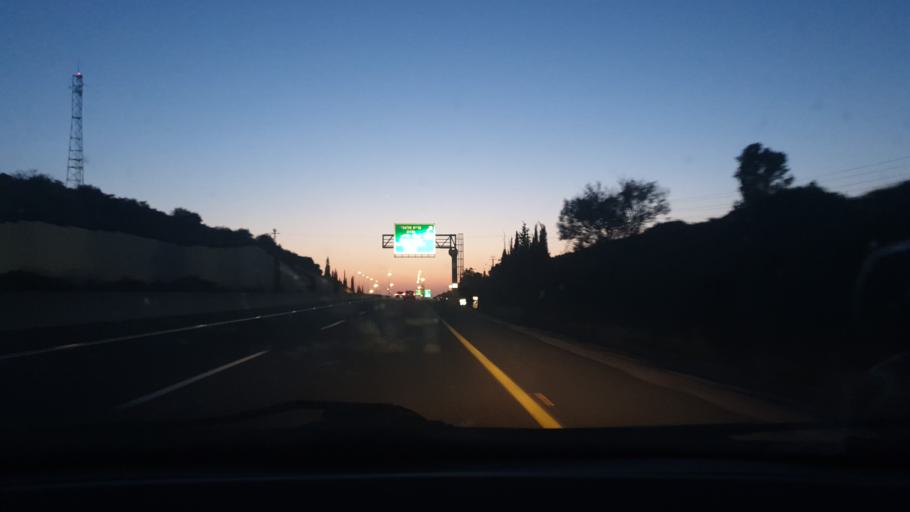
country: IL
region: Central District
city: Gedera
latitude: 31.7999
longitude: 34.7776
